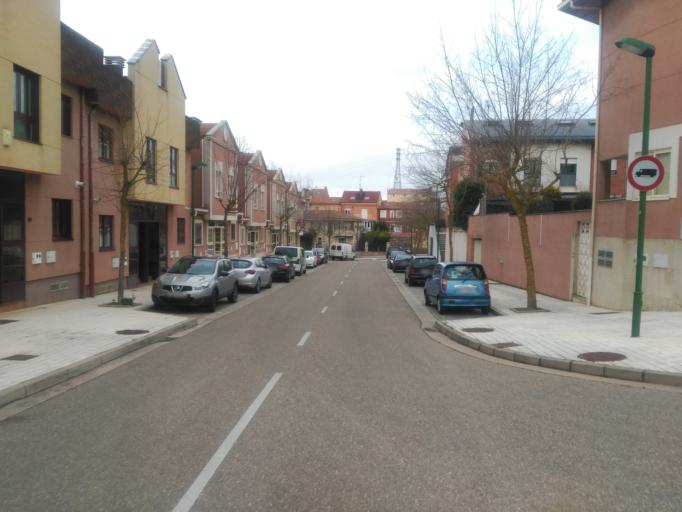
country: ES
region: Castille and Leon
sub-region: Provincia de Burgos
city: Burgos
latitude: 42.3372
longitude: -3.6877
